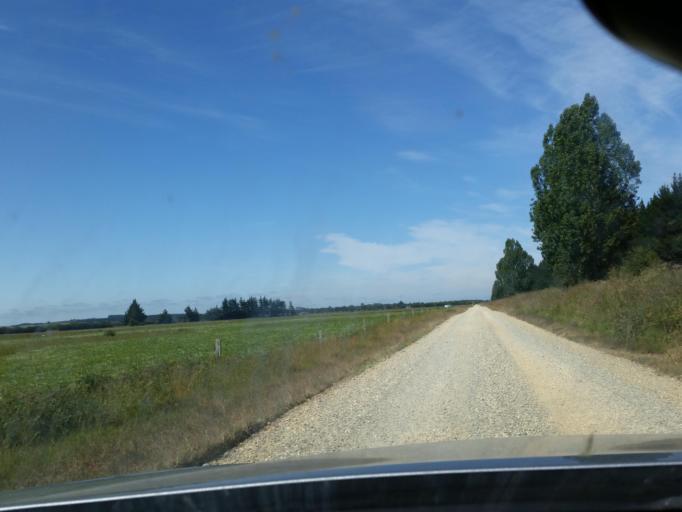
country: NZ
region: Southland
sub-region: Southland District
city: Winton
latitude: -46.2259
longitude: 168.4900
